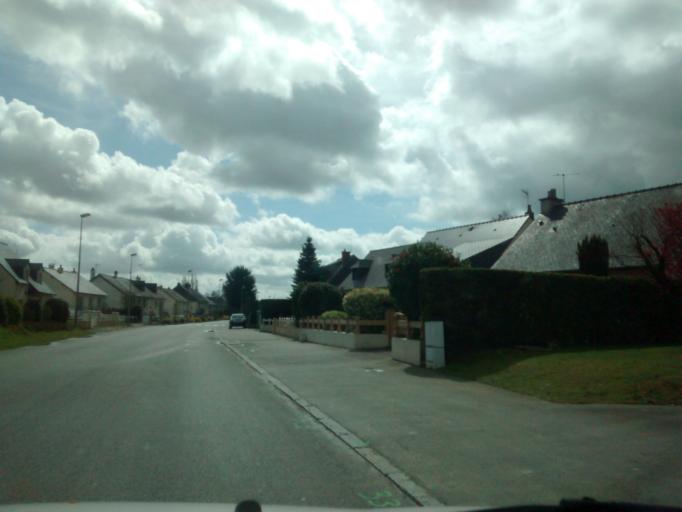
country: FR
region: Brittany
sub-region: Departement d'Ille-et-Vilaine
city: Livre-sur-Changeon
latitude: 48.2227
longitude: -1.3478
